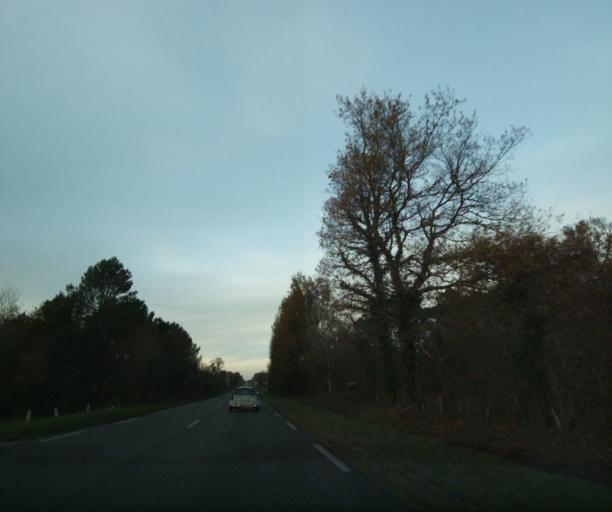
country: FR
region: Aquitaine
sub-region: Departement de la Gironde
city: Bazas
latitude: 44.4868
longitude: -0.2326
